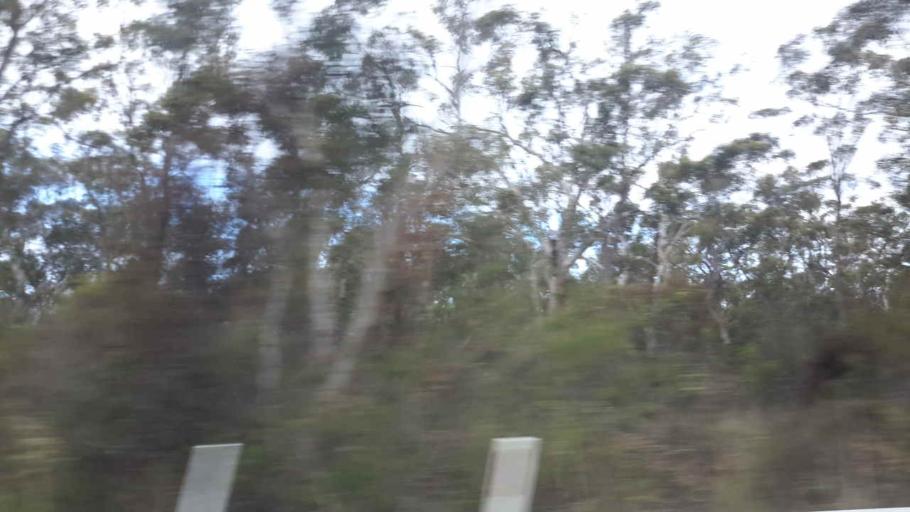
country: AU
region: New South Wales
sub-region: Wollondilly
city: Douglas Park
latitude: -34.2270
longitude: 150.8142
